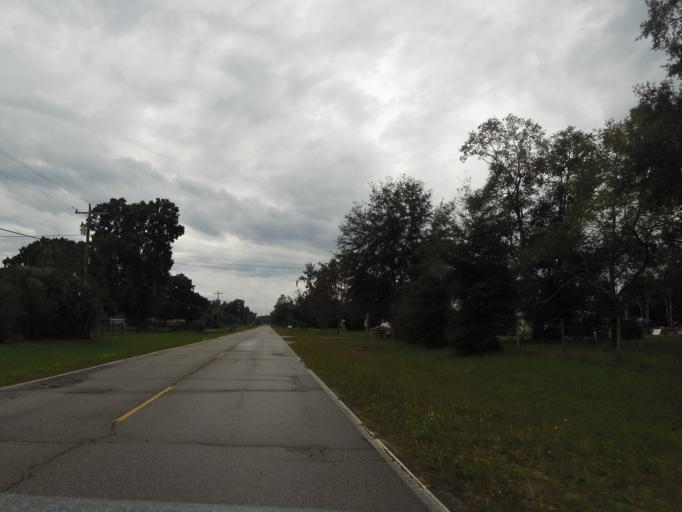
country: US
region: Florida
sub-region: Clay County
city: Middleburg
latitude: 30.1182
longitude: -81.9618
